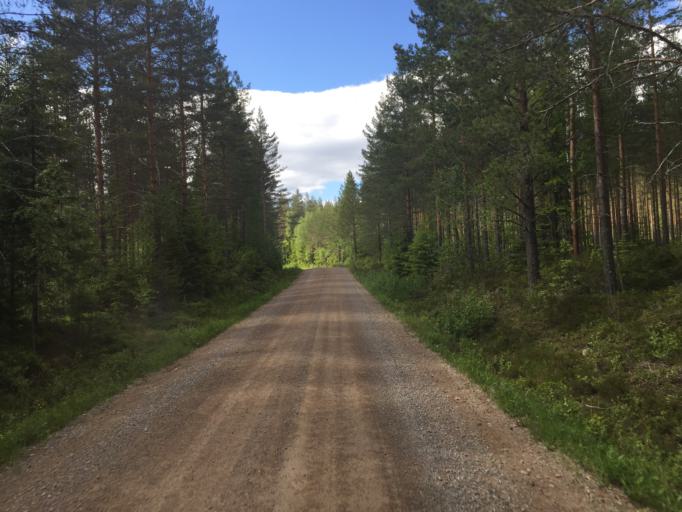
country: SE
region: Dalarna
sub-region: Vansbro Kommun
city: Vansbro
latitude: 60.4496
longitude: 14.1572
